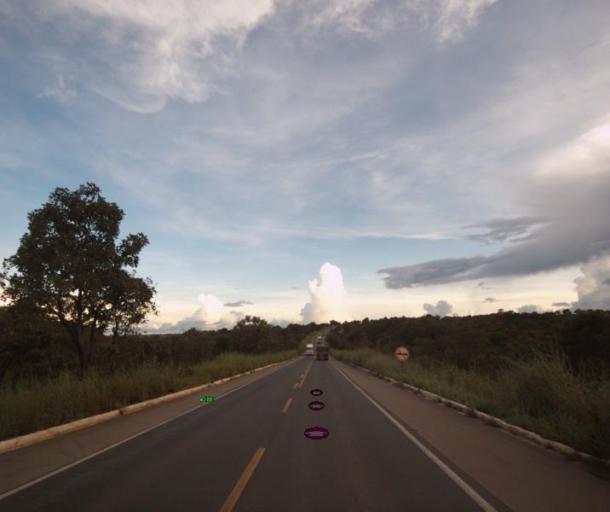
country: BR
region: Goias
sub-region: Uruacu
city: Uruacu
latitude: -14.2260
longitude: -49.1331
